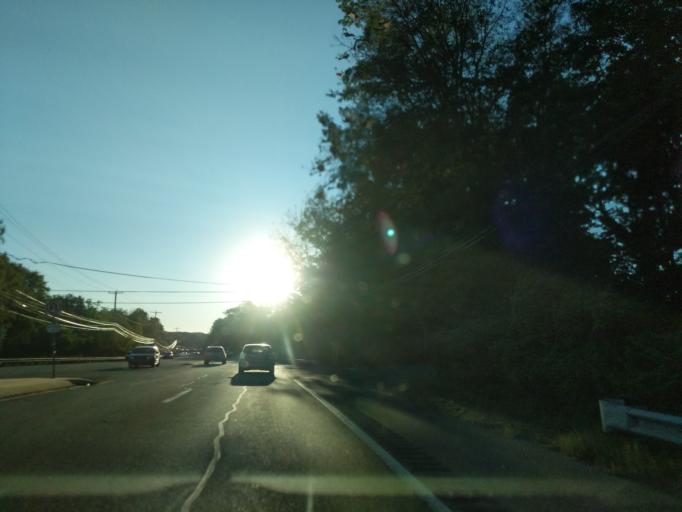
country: US
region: Pennsylvania
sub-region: Chester County
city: West Chester
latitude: 39.8732
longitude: -75.5823
